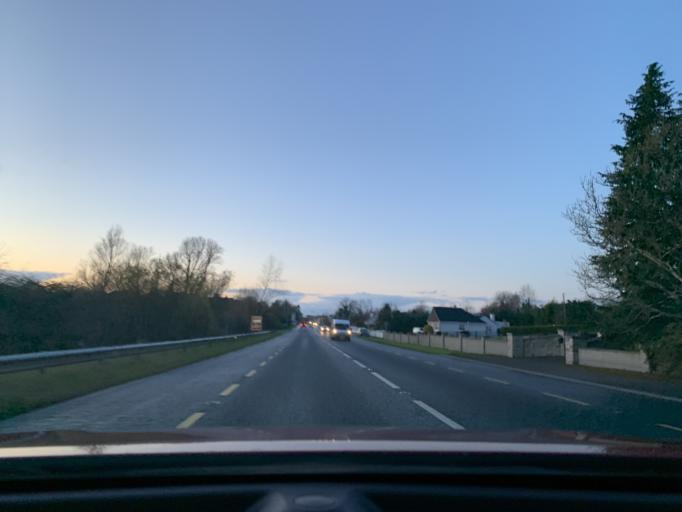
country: IE
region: Connaught
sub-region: County Leitrim
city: Carrick-on-Shannon
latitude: 53.9411
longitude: -8.0655
